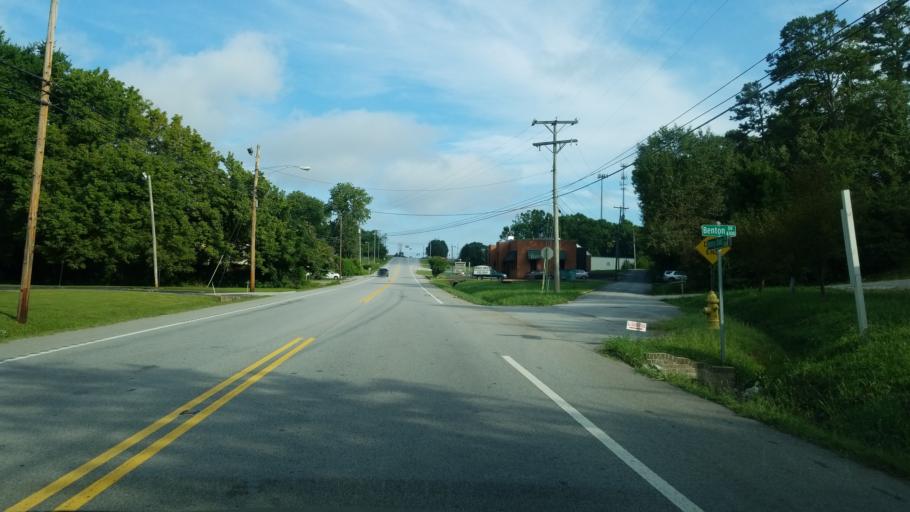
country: US
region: Tennessee
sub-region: Hamilton County
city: East Chattanooga
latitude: 35.0776
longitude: -85.2065
